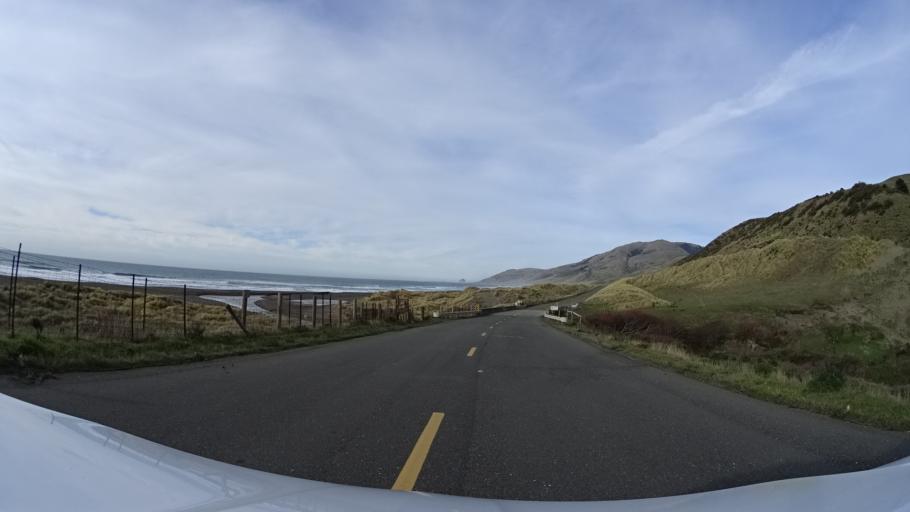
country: US
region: California
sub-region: Humboldt County
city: Ferndale
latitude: 40.3521
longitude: -124.3606
